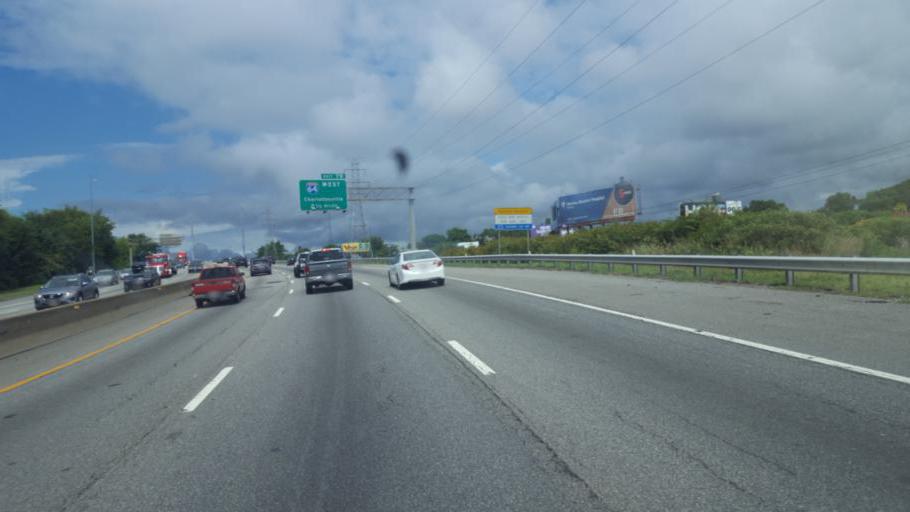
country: US
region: Virginia
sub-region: City of Richmond
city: Richmond
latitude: 37.5567
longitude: -77.4482
